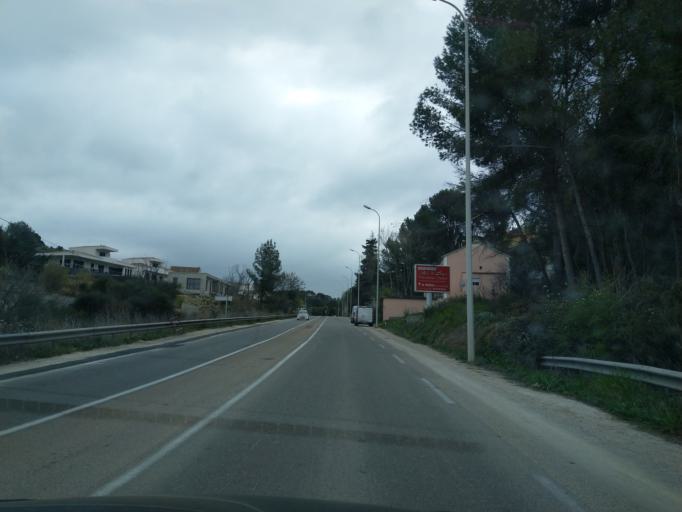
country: FR
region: Provence-Alpes-Cote d'Azur
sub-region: Departement des Bouches-du-Rhone
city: Allauch
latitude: 43.3194
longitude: 5.4686
